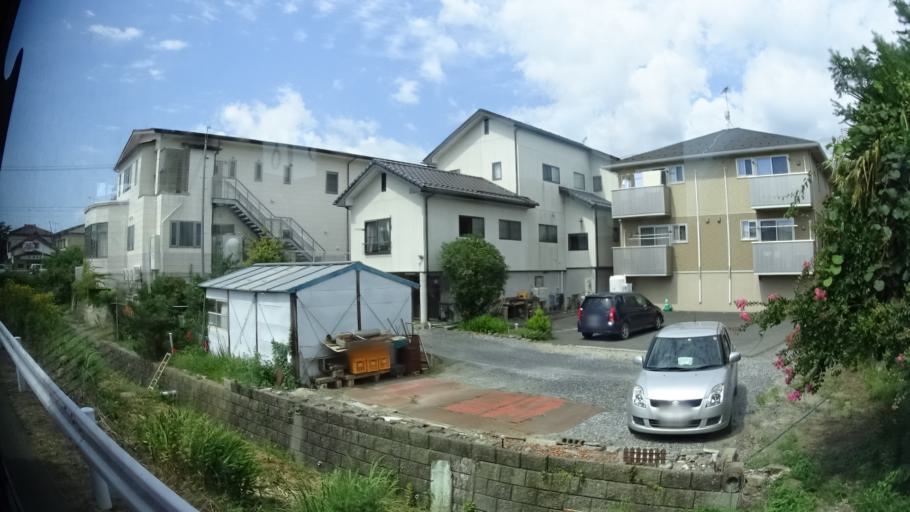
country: JP
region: Iwate
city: Ofunato
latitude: 38.8430
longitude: 141.5815
